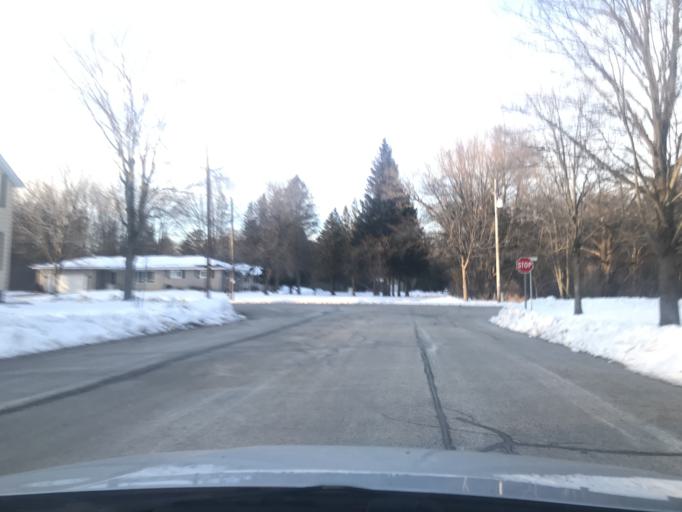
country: US
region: Wisconsin
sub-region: Marinette County
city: Peshtigo
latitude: 45.0592
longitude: -87.7402
